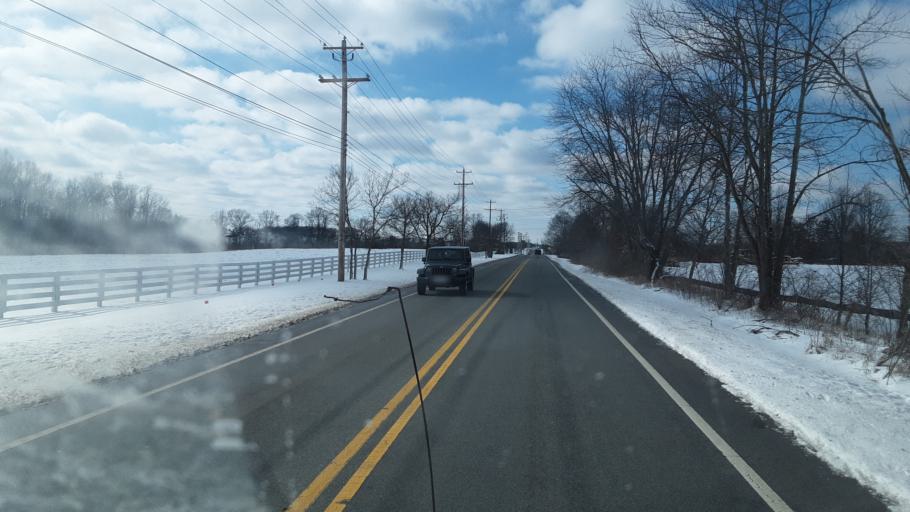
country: US
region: Ohio
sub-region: Franklin County
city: New Albany
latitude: 40.0798
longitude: -82.8391
